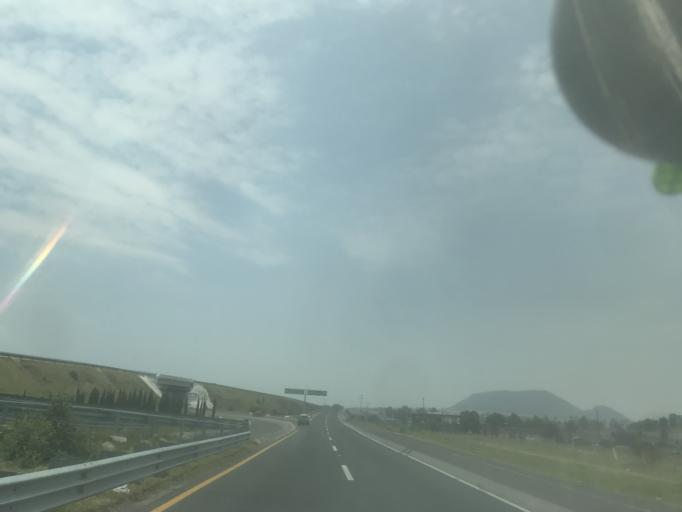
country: MX
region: Mexico
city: Amecameca de Juarez
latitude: 19.1178
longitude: -98.7837
